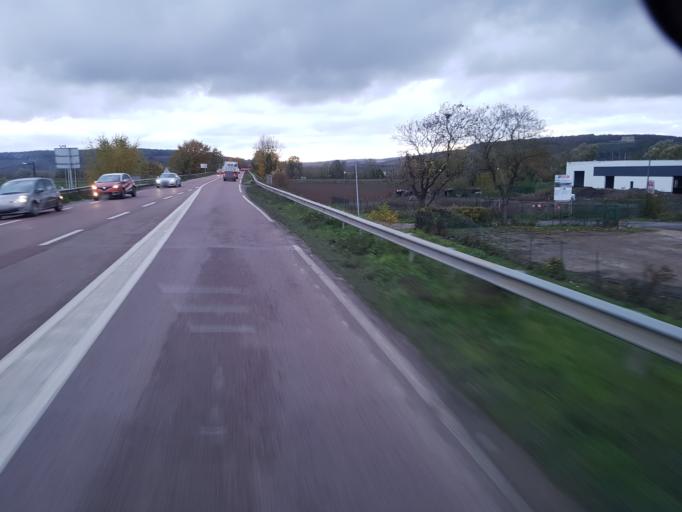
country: FR
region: Picardie
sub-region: Departement de l'Aisne
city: Etampes-sur-Marne
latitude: 49.0354
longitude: 3.4051
